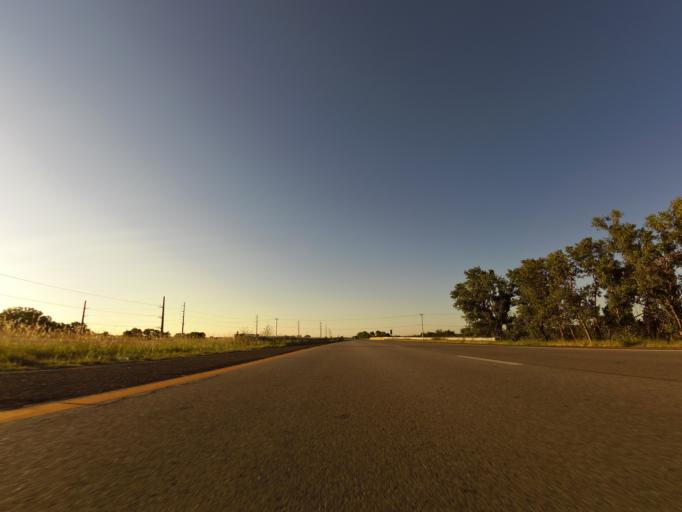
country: US
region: Kansas
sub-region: Sedgwick County
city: Maize
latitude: 37.7821
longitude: -97.4615
